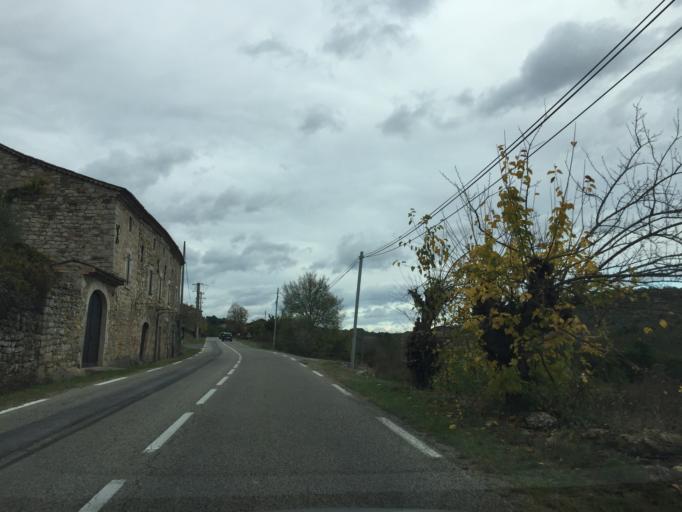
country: FR
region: Rhone-Alpes
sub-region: Departement de l'Ardeche
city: Les Vans
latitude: 44.4197
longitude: 4.1764
